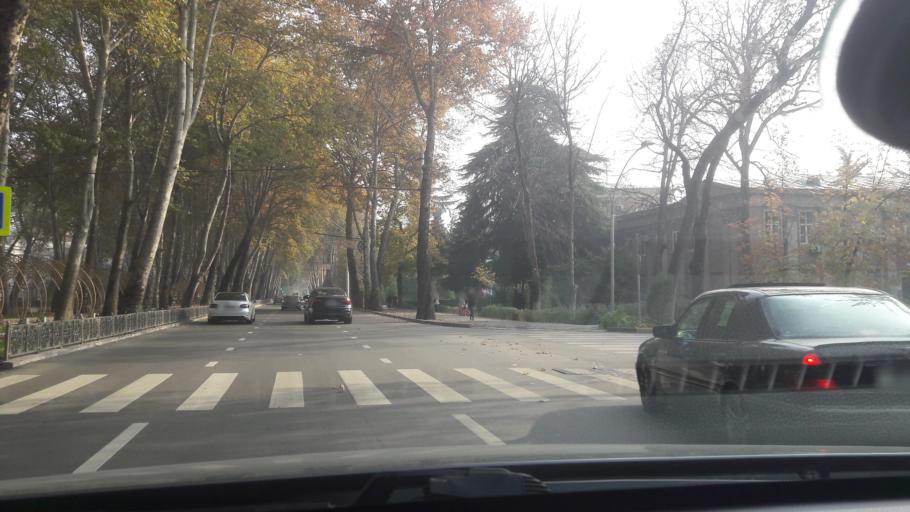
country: TJ
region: Dushanbe
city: Dushanbe
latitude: 38.5699
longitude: 68.7907
